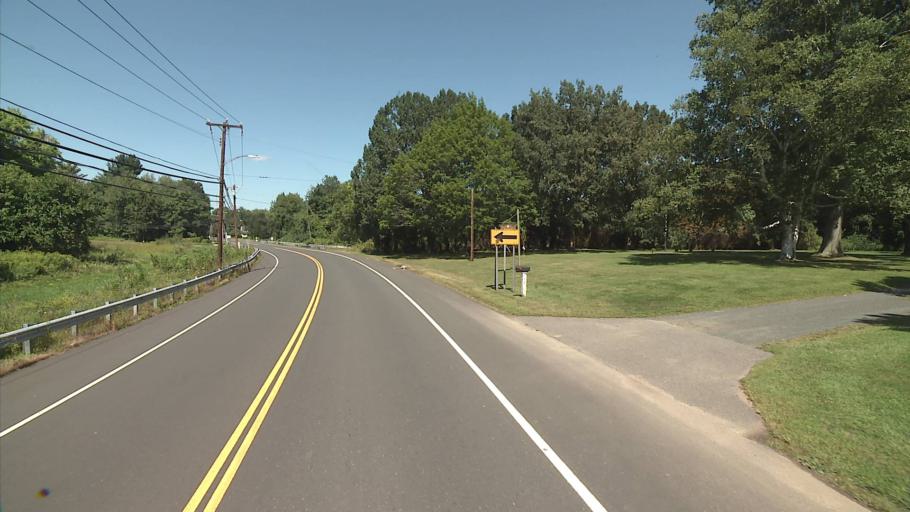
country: US
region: Connecticut
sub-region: Hartford County
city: Windsor
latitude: 41.8789
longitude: -72.6247
